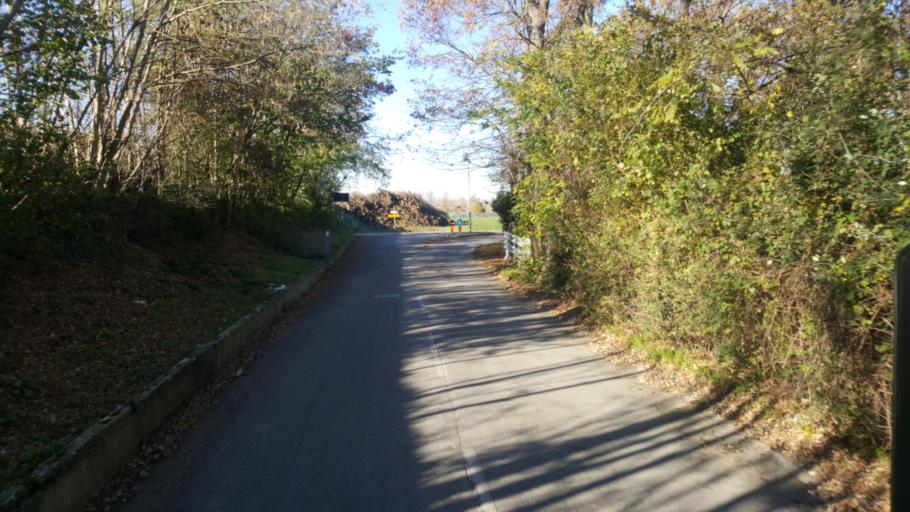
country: IT
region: Emilia-Romagna
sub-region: Provincia di Bologna
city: Calderara di Reno
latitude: 44.5477
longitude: 11.2834
